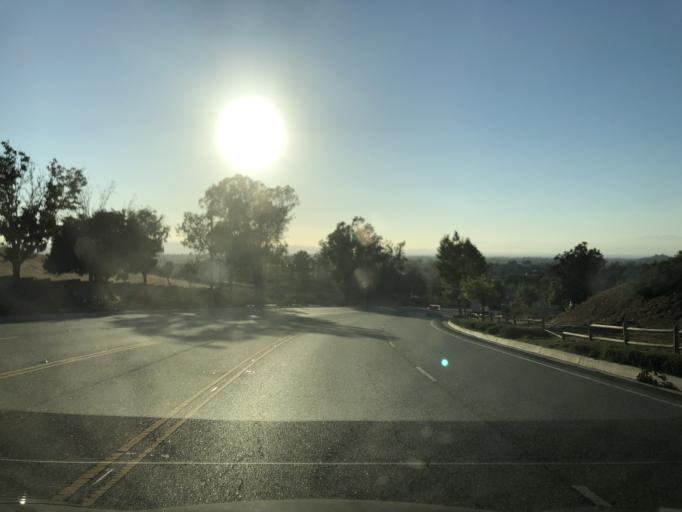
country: US
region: California
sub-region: Riverside County
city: Corona
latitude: 33.8963
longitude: -117.5510
